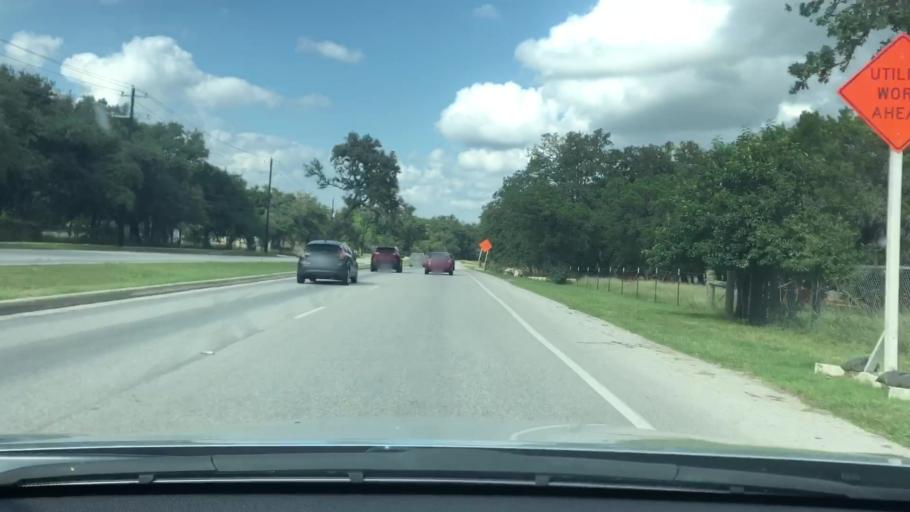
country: US
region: Texas
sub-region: Kendall County
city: Boerne
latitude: 29.7843
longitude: -98.7176
